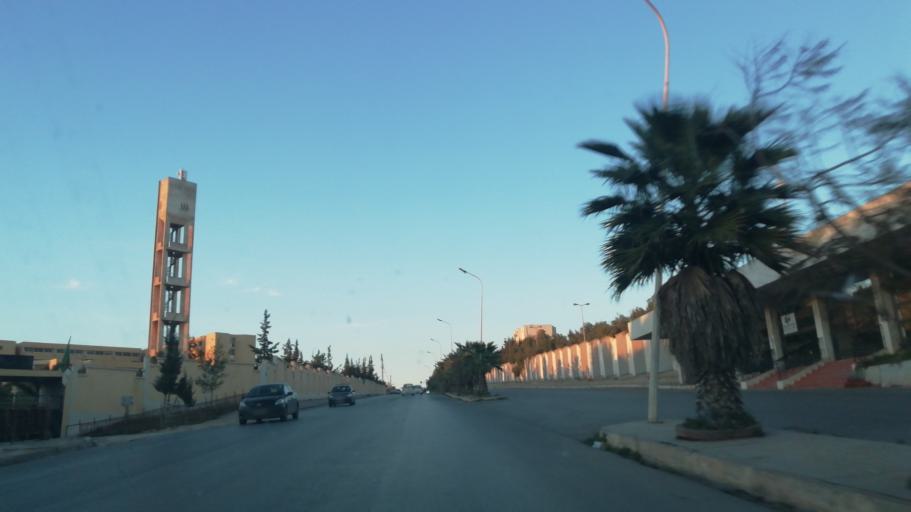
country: DZ
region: Oran
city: Bir el Djir
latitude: 35.6995
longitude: -0.5853
